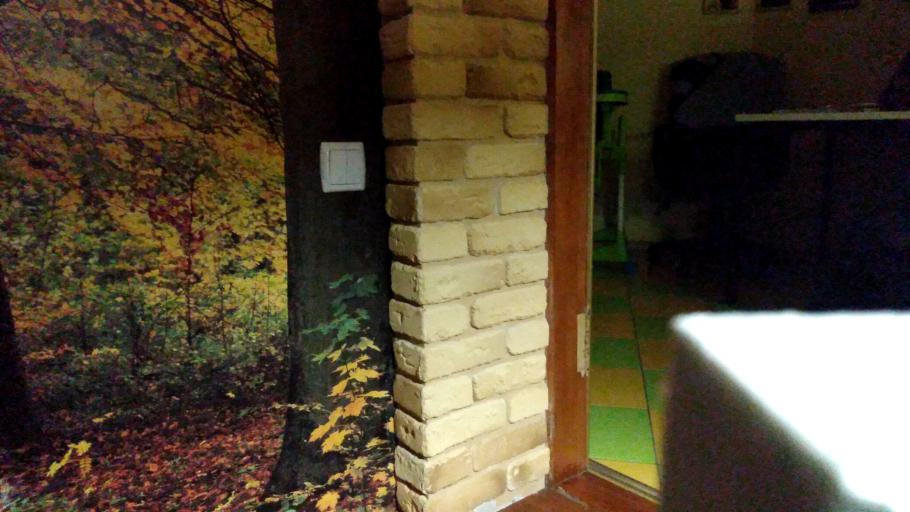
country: RU
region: Vologda
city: Lipin Bor
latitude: 60.9981
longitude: 37.9615
